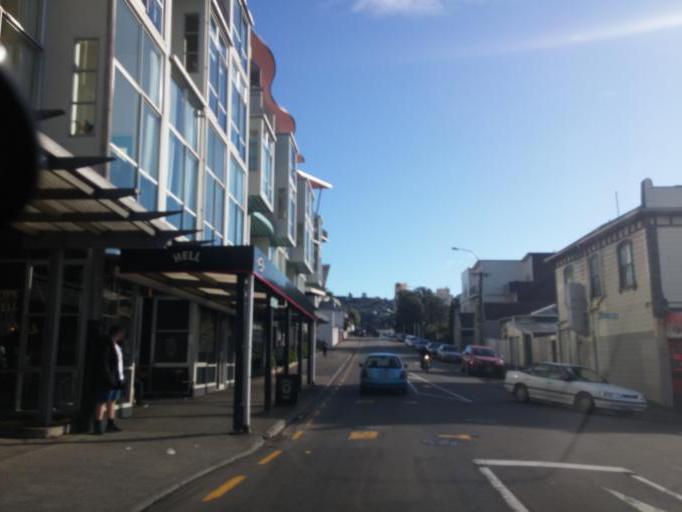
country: NZ
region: Wellington
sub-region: Wellington City
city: Wellington
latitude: -41.2978
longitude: 174.7734
